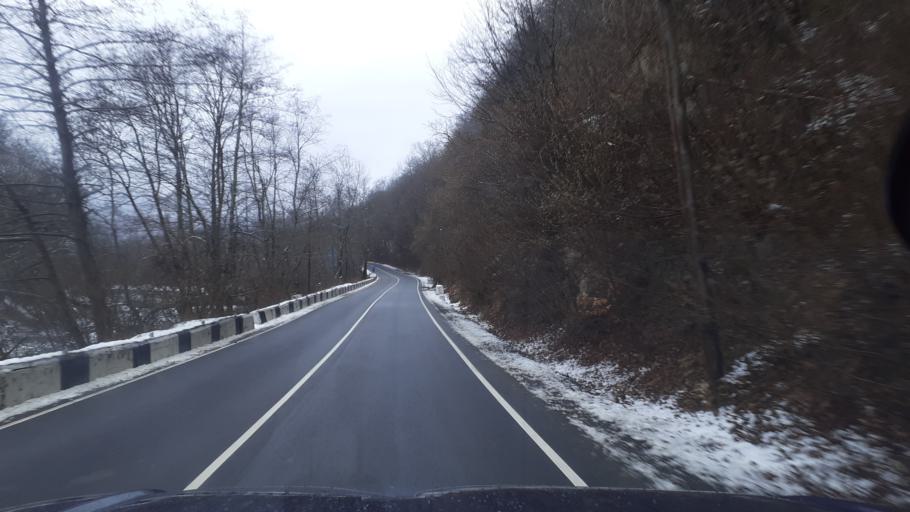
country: RU
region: Adygeya
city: Kamennomostskiy
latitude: 44.1192
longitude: 40.1221
